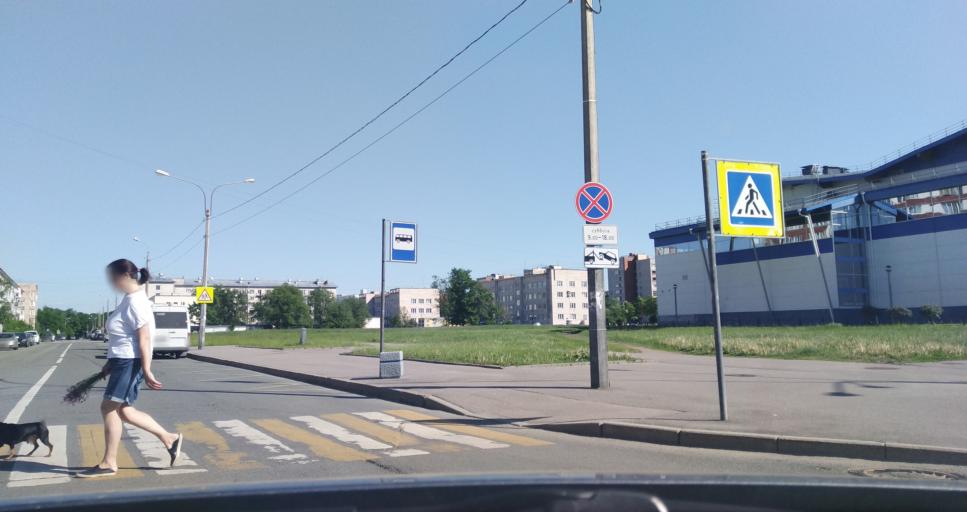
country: RU
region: St.-Petersburg
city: Krasnoye Selo
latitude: 59.7436
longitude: 30.0861
